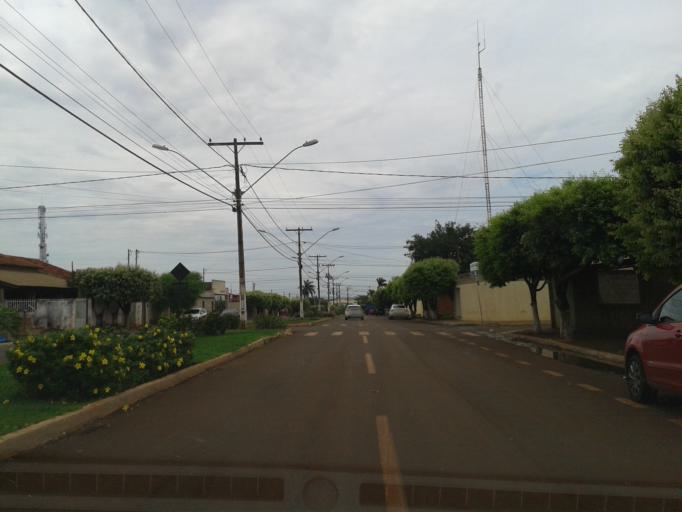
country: BR
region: Goias
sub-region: Itumbiara
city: Itumbiara
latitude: -18.4292
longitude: -49.1882
